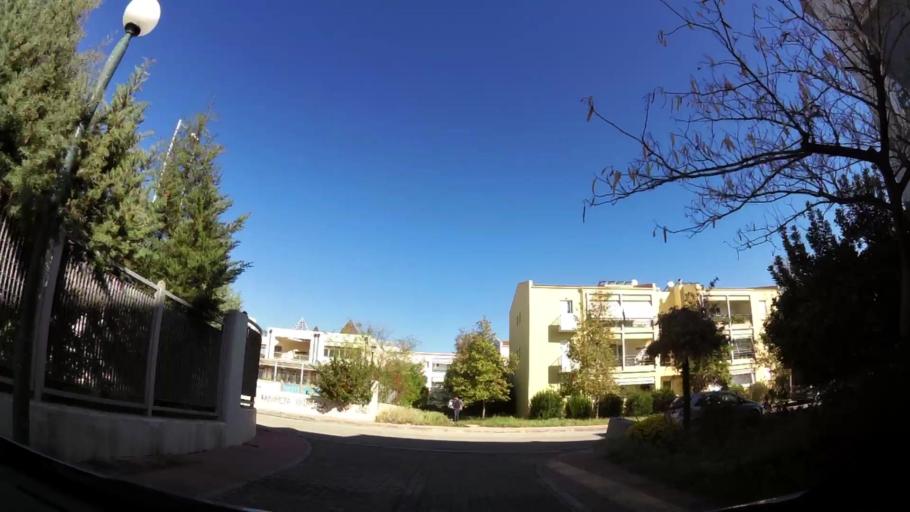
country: GR
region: Attica
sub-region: Nomarchia Anatolikis Attikis
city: Varybobi
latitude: 38.1090
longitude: 23.7709
